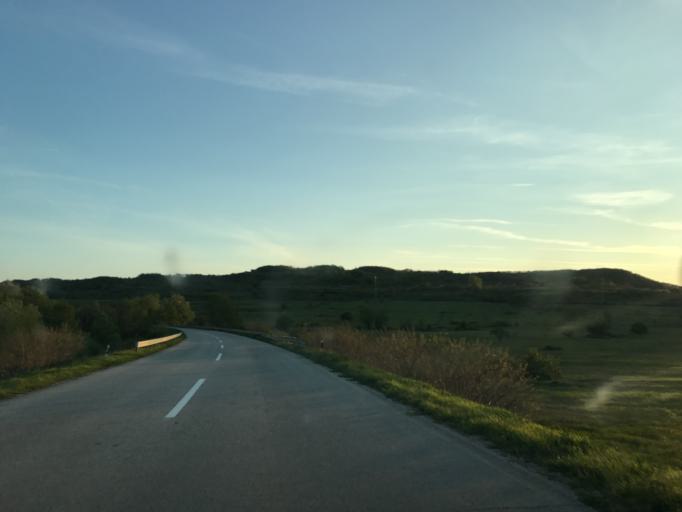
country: RO
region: Mehedinti
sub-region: Comuna Gogosu
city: Ostrovu Mare
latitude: 44.3998
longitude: 22.4668
